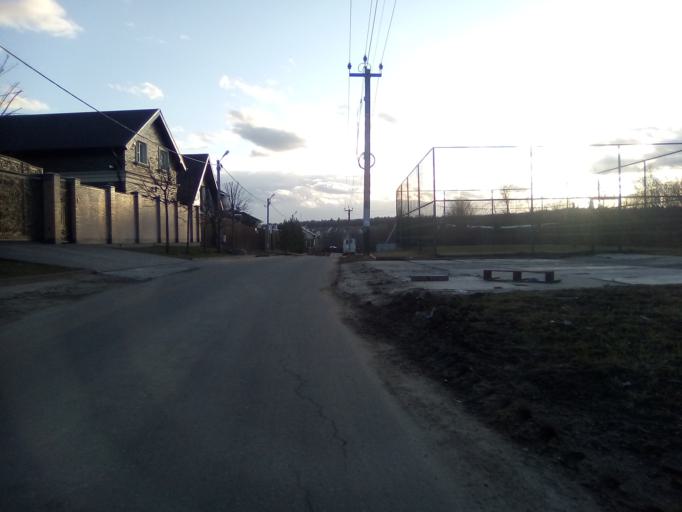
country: RU
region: Moskovskaya
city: Filimonki
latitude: 55.5789
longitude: 37.3487
